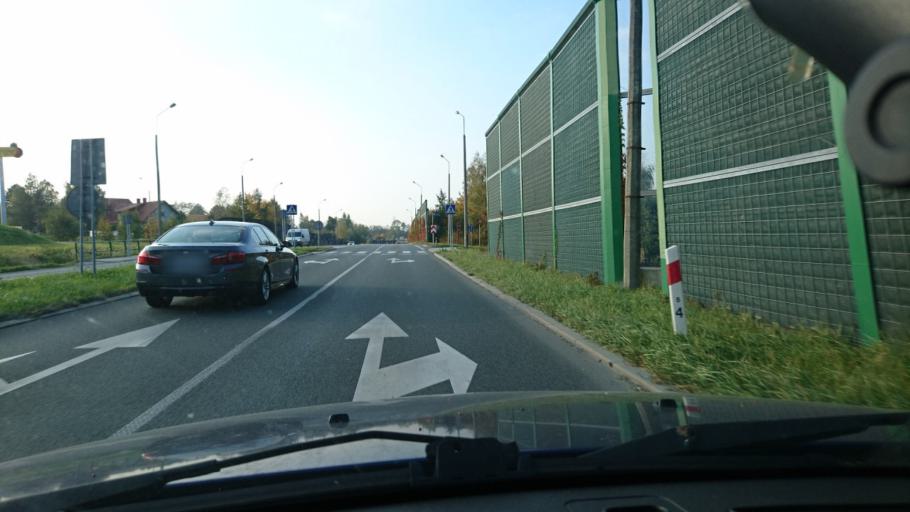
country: PL
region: Silesian Voivodeship
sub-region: Powiat cieszynski
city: Ustron
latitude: 49.7167
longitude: 18.8023
